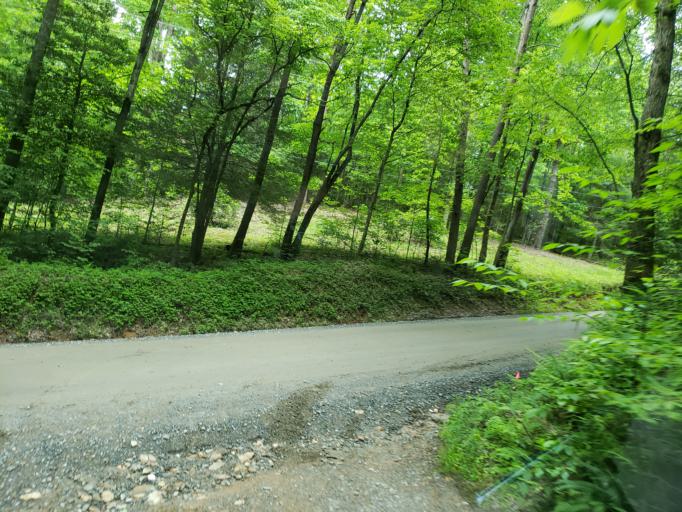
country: US
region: Georgia
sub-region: Fannin County
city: Blue Ridge
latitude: 34.8504
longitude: -84.4180
